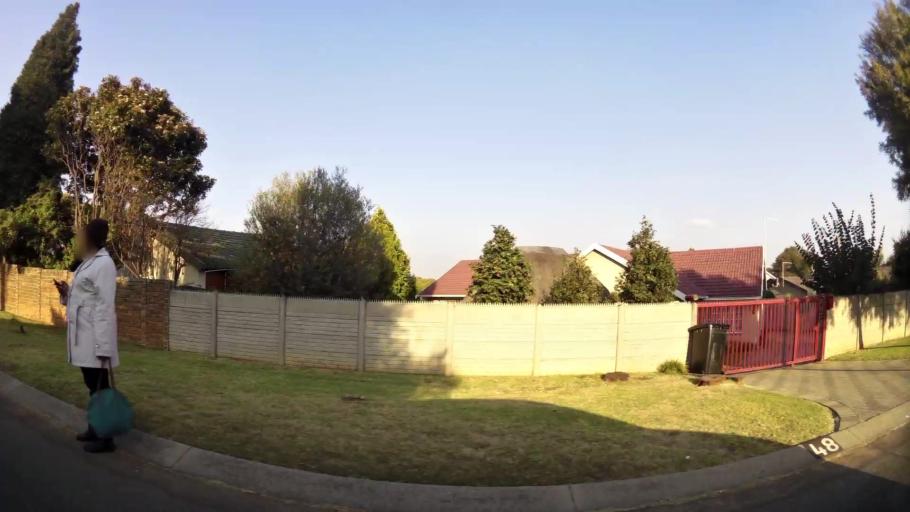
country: ZA
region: Gauteng
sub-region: City of Johannesburg Metropolitan Municipality
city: Modderfontein
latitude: -26.0776
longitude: 28.2218
